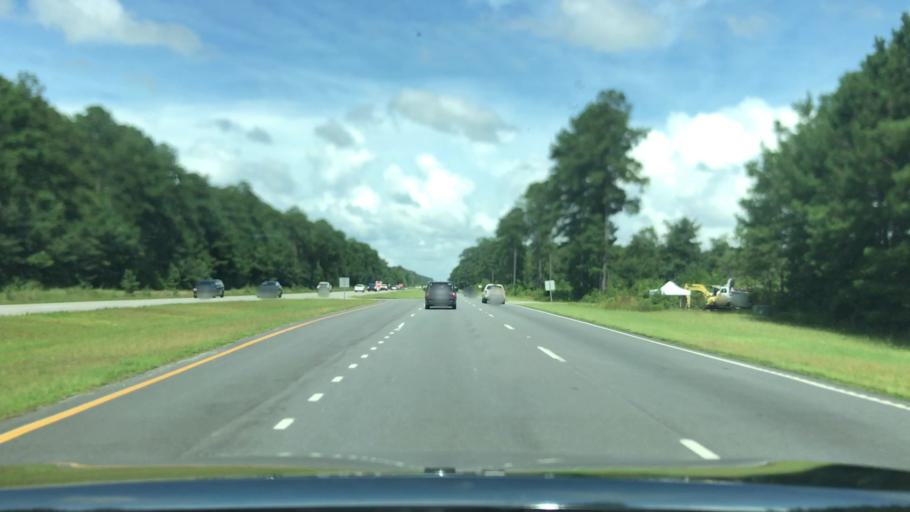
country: US
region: South Carolina
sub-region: Jasper County
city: Hardeeville
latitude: 32.3037
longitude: -81.0295
